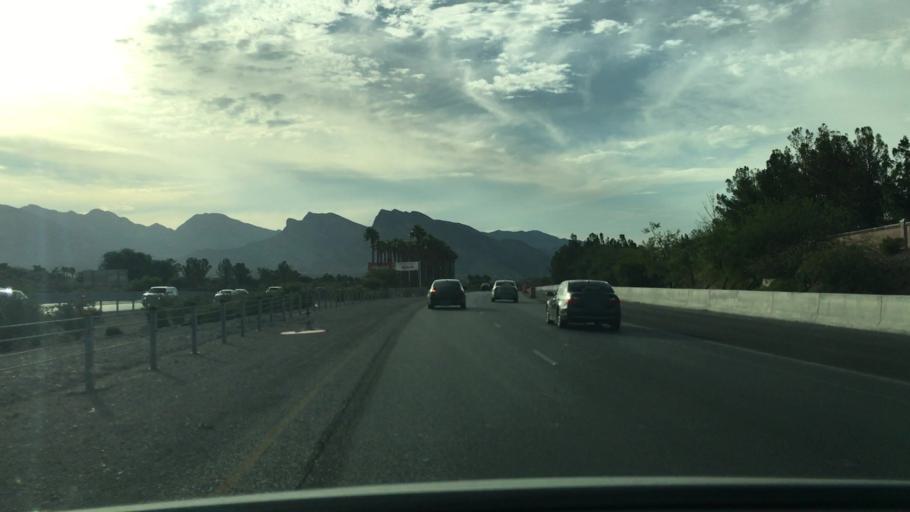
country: US
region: Nevada
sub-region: Clark County
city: Summerlin South
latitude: 36.1798
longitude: -115.2966
